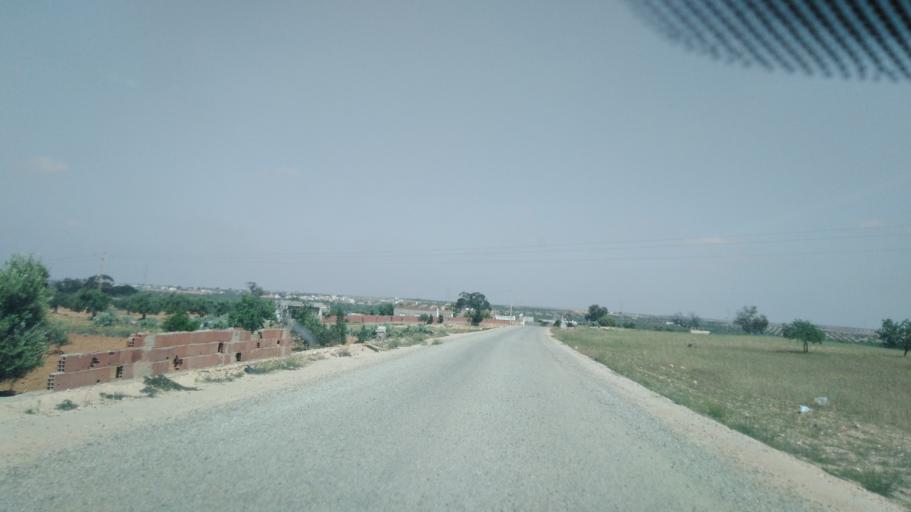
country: TN
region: Safaqis
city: Sfax
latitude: 34.7278
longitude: 10.5724
